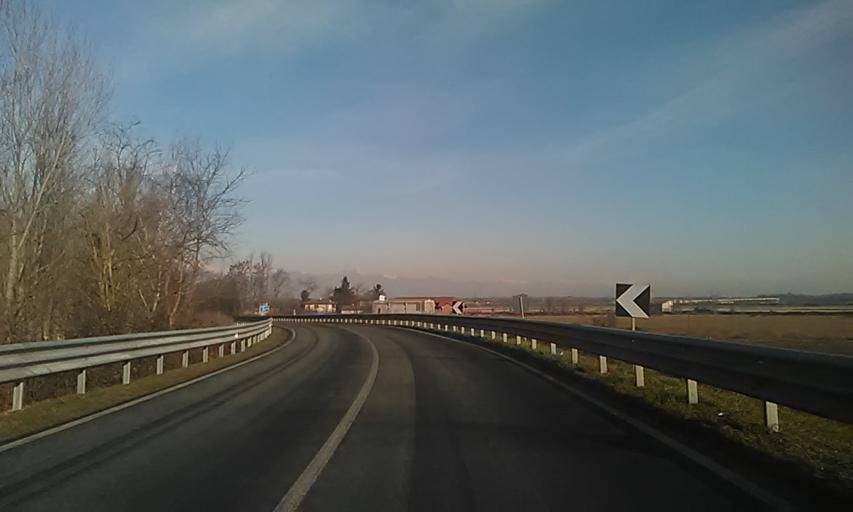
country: IT
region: Piedmont
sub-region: Provincia di Vercelli
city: Formigliana
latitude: 45.4345
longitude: 8.2969
